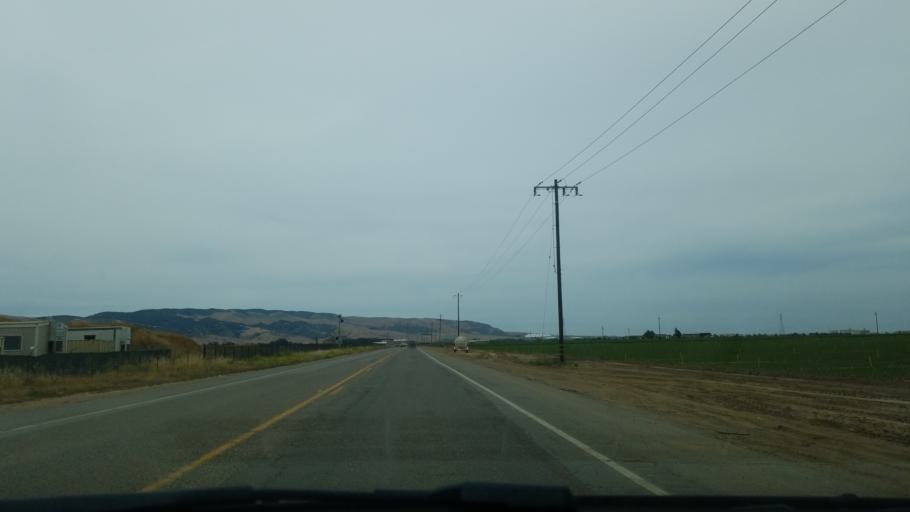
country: US
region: California
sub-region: Santa Barbara County
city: Santa Maria
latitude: 34.9208
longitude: -120.4910
